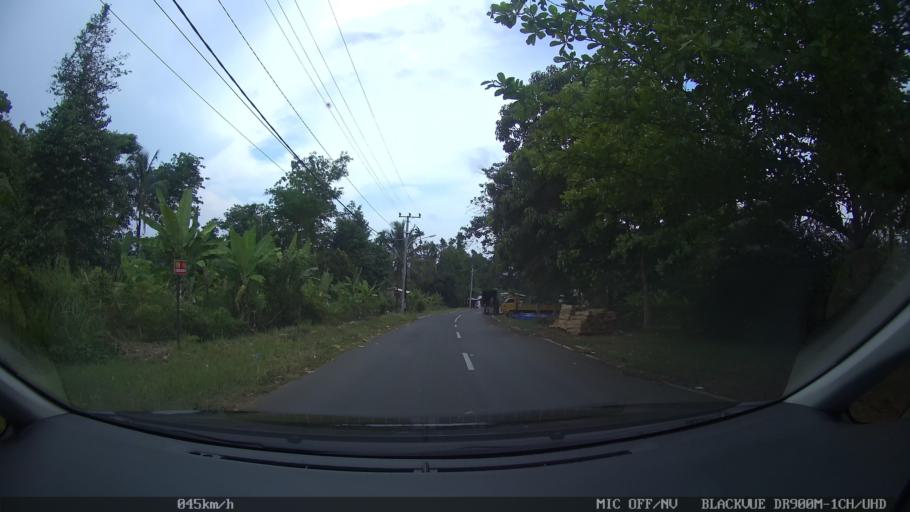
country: ID
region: Lampung
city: Bandarlampung
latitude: -5.4216
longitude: 105.1926
